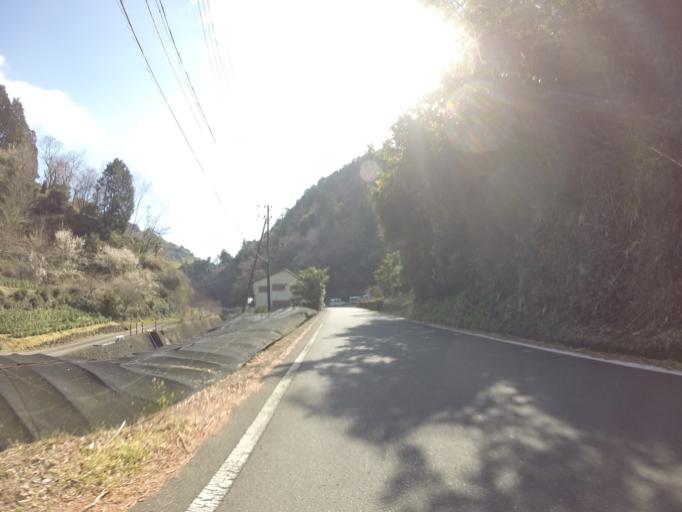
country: JP
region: Shizuoka
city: Shizuoka-shi
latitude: 35.0829
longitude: 138.4726
